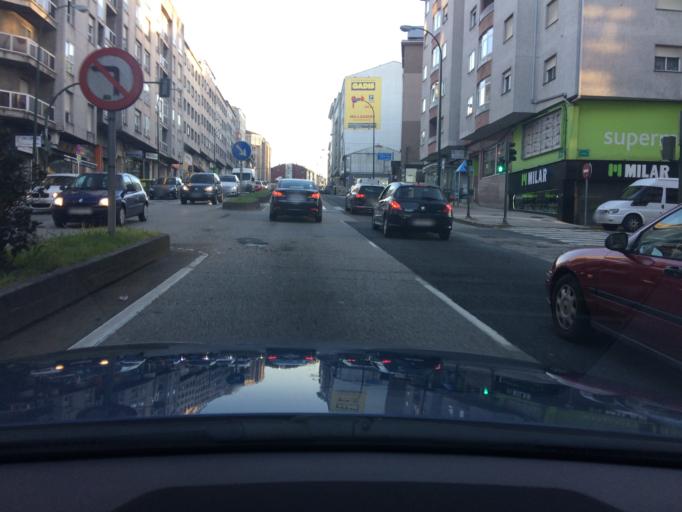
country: ES
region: Galicia
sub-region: Provincia da Coruna
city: Santiago de Compostela
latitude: 42.8450
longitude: -8.5764
